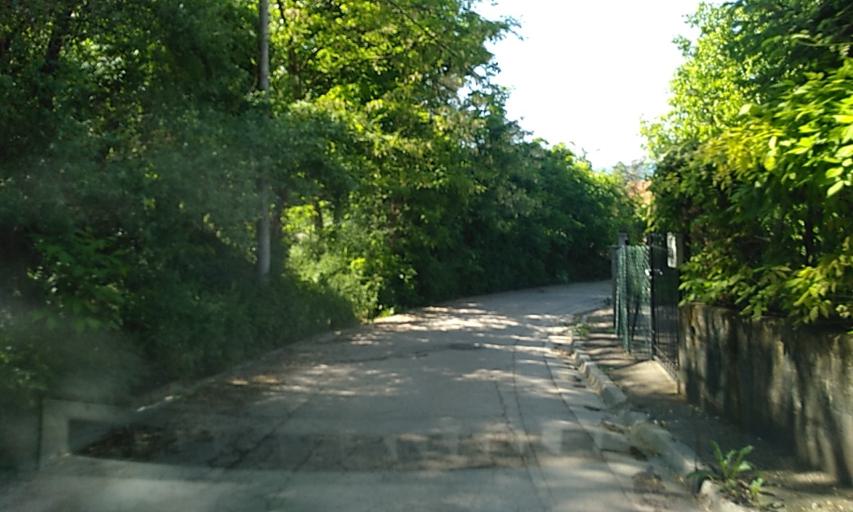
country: RS
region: Central Serbia
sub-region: Nisavski Okrug
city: Niska Banja
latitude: 43.2931
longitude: 22.0151
